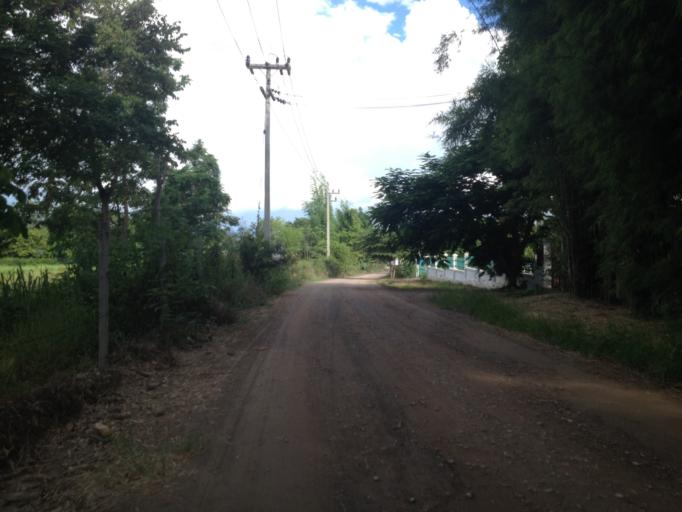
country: TH
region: Chiang Mai
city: Hang Dong
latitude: 18.7000
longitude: 98.8941
